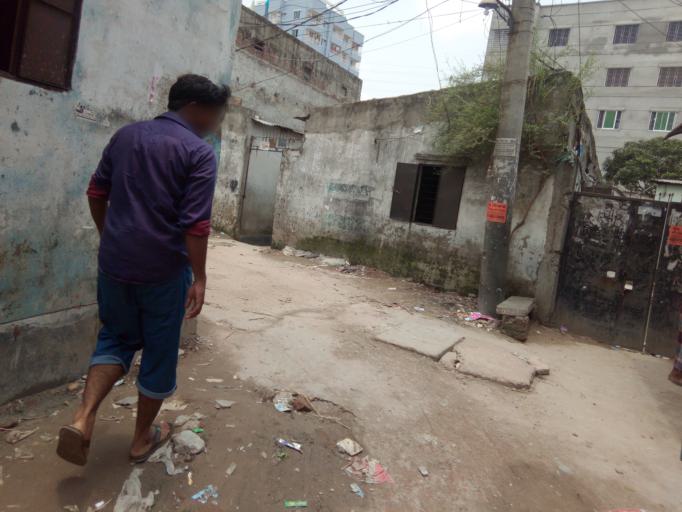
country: BD
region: Dhaka
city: Paltan
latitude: 23.7687
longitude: 90.4308
